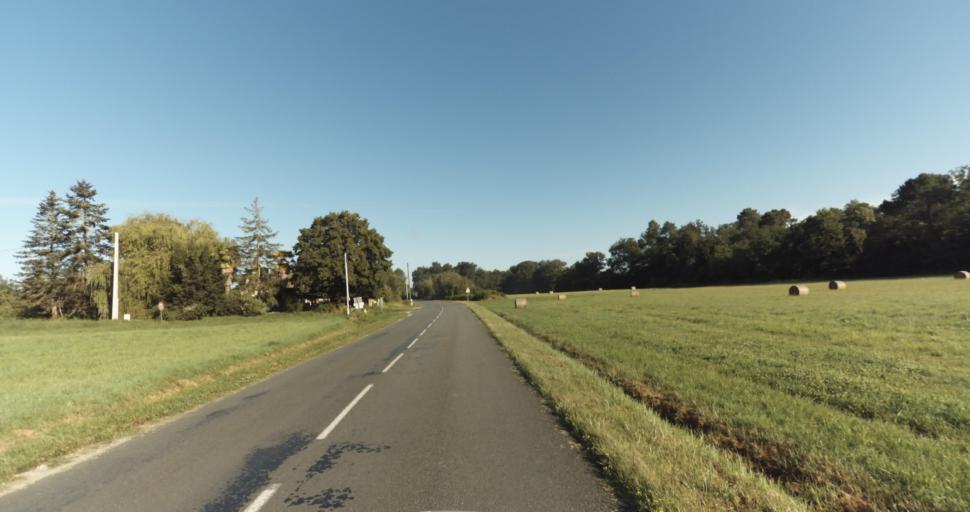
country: FR
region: Aquitaine
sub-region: Departement de la Gironde
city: Bazas
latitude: 44.4115
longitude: -0.2122
